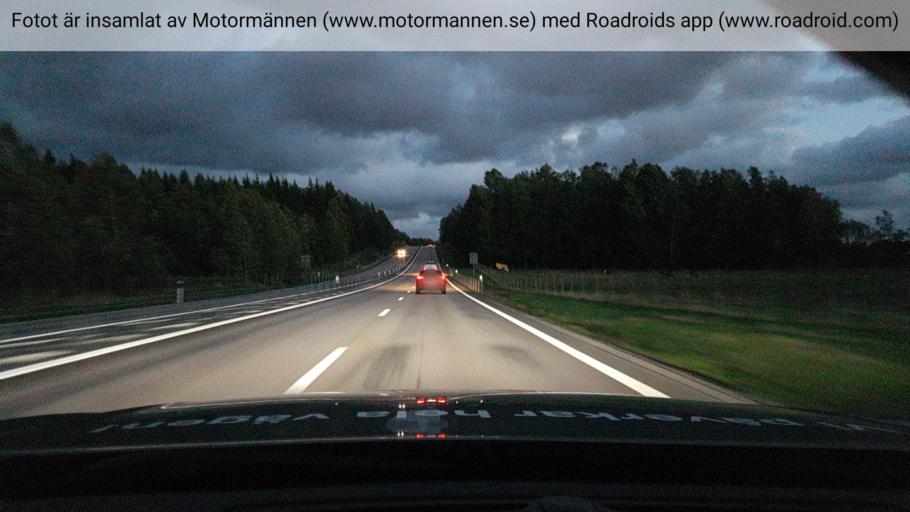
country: SE
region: Vaermland
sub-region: Kristinehamns Kommun
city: Kristinehamn
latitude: 59.3494
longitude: 14.0803
